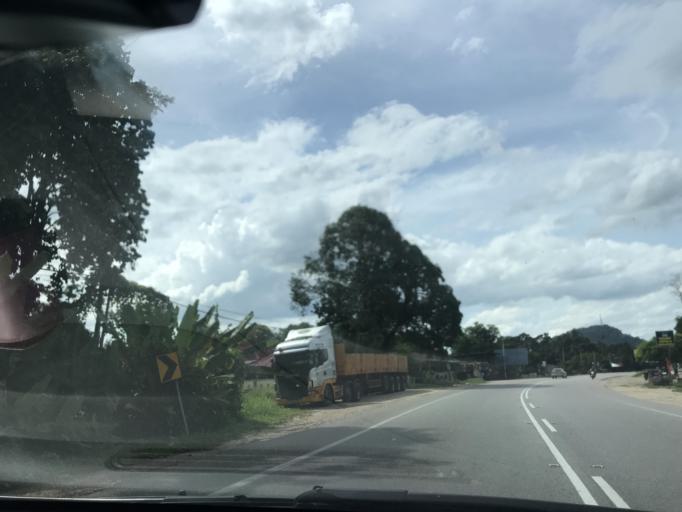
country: MY
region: Kelantan
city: Pulai Chondong
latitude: 5.8658
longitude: 102.1686
